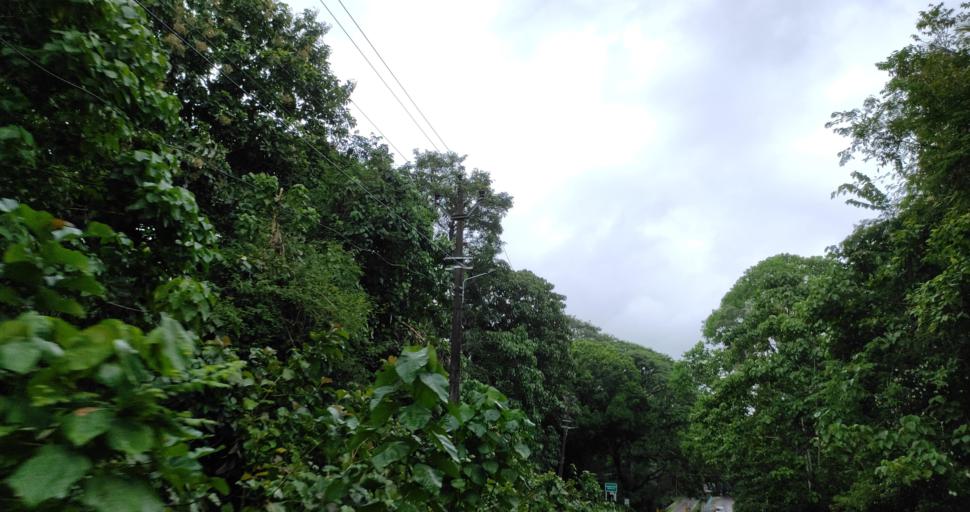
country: IN
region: Kerala
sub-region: Ernakulam
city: Angamali
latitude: 10.2876
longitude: 76.5539
